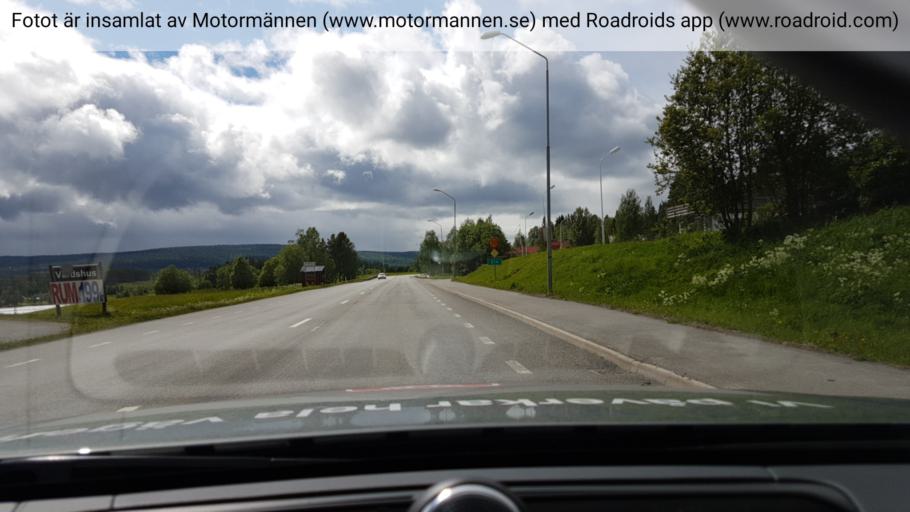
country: SE
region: Jaemtland
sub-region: Are Kommun
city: Jarpen
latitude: 63.3099
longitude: 13.6459
